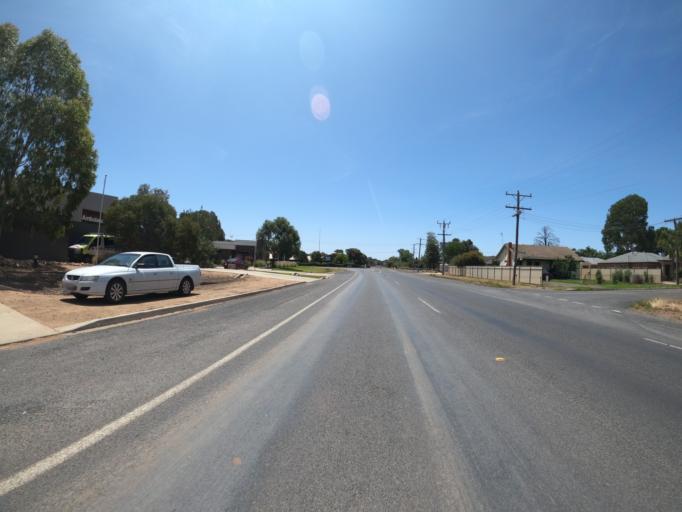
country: AU
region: Victoria
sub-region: Moira
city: Yarrawonga
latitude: -36.0214
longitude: 145.9955
